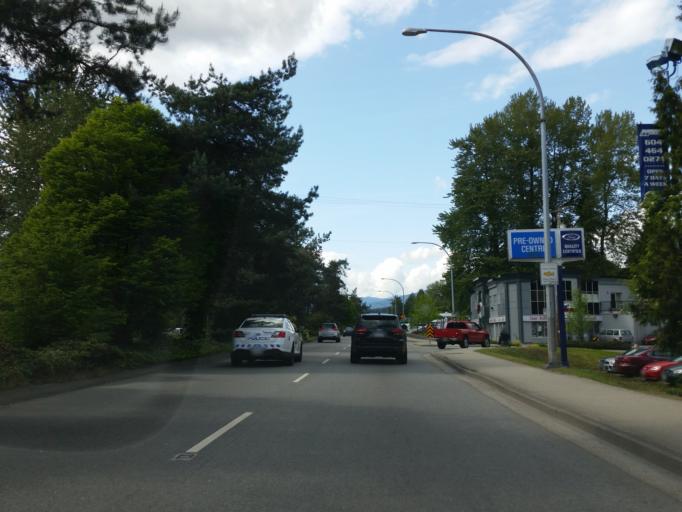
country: CA
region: British Columbia
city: Coquitlam
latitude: 49.2708
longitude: -122.7840
